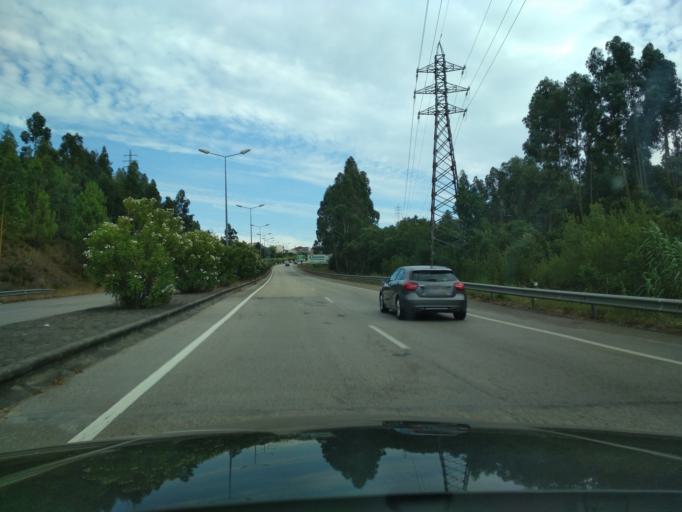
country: PT
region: Coimbra
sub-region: Coimbra
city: Coimbra
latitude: 40.2194
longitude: -8.3954
